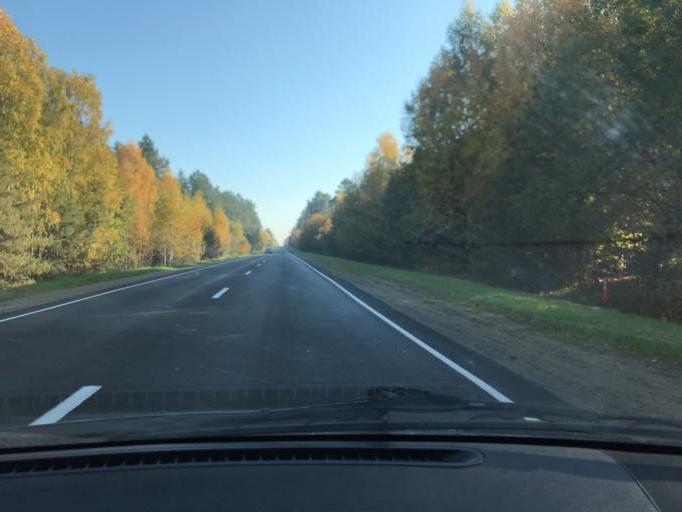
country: BY
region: Brest
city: Lyakhavichy
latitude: 52.9586
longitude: 26.3613
